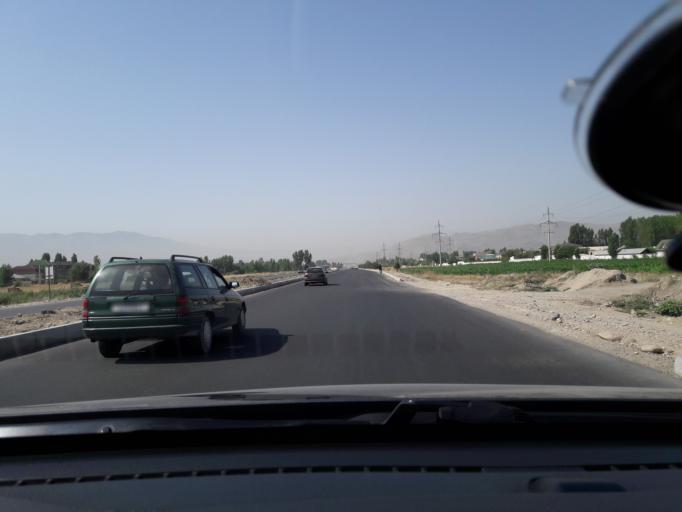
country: TJ
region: Dushanbe
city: Dushanbe
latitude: 38.4919
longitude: 68.7520
